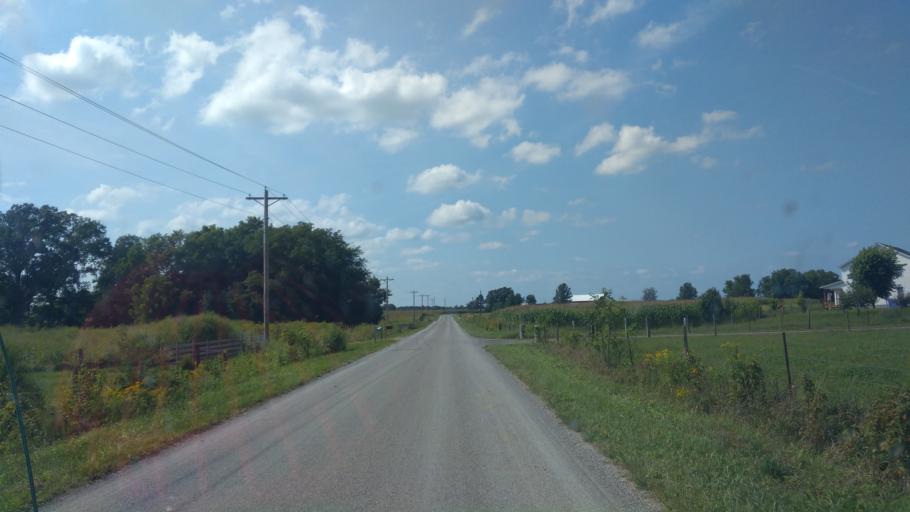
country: US
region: Ohio
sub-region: Hardin County
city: Kenton
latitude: 40.5648
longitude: -83.4465
